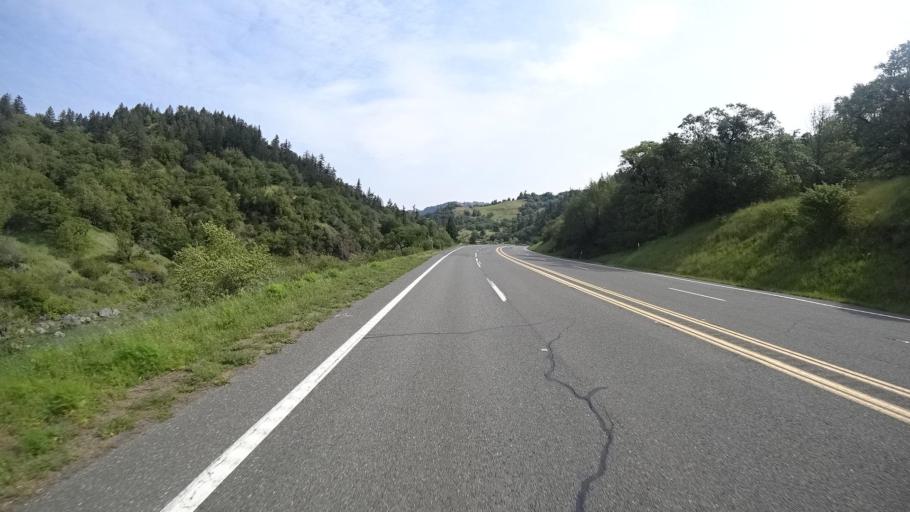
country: US
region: California
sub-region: Humboldt County
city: Redway
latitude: 40.1643
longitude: -123.7858
